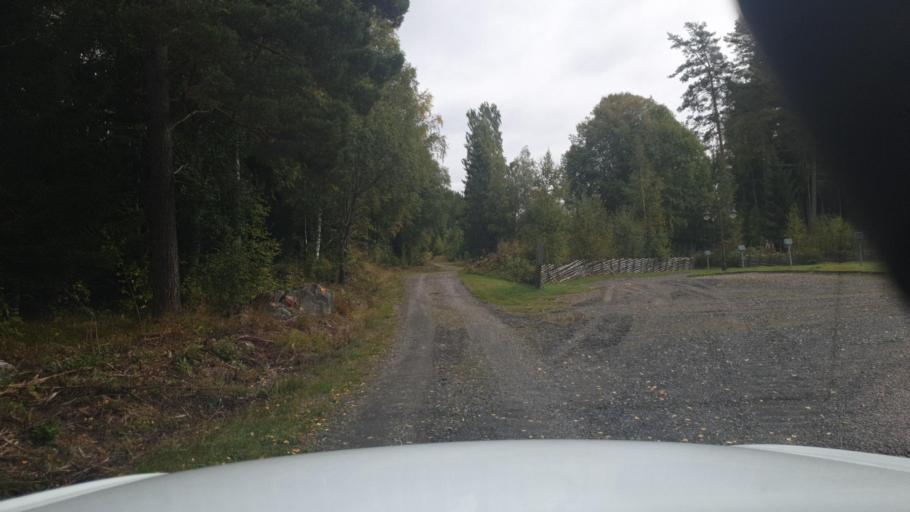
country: SE
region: Vaermland
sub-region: Eda Kommun
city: Charlottenberg
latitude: 60.0914
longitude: 12.5149
